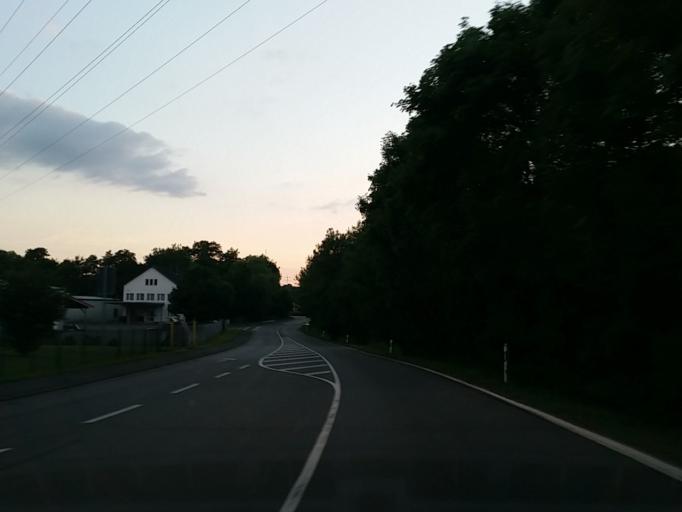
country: DE
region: Saarland
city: Wadern
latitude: 49.5281
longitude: 6.8998
